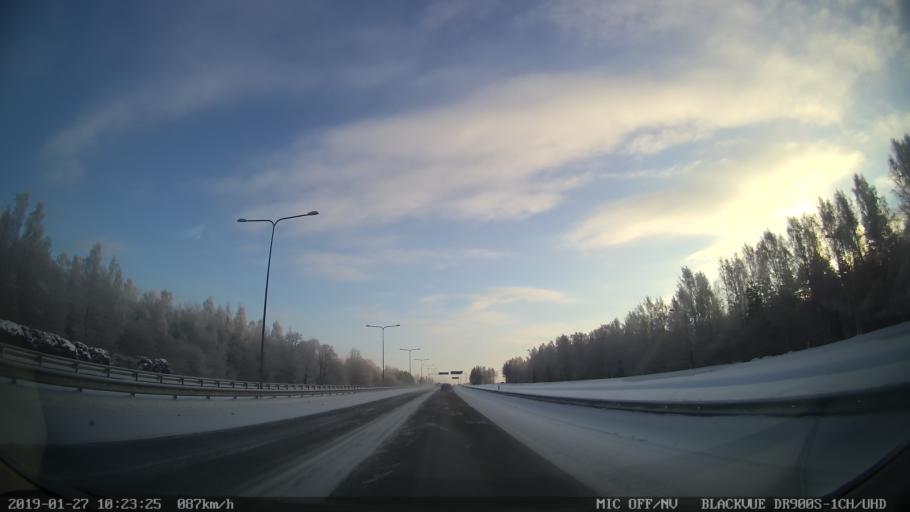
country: EE
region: Harju
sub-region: Maardu linn
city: Maardu
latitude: 59.4525
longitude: 25.0184
